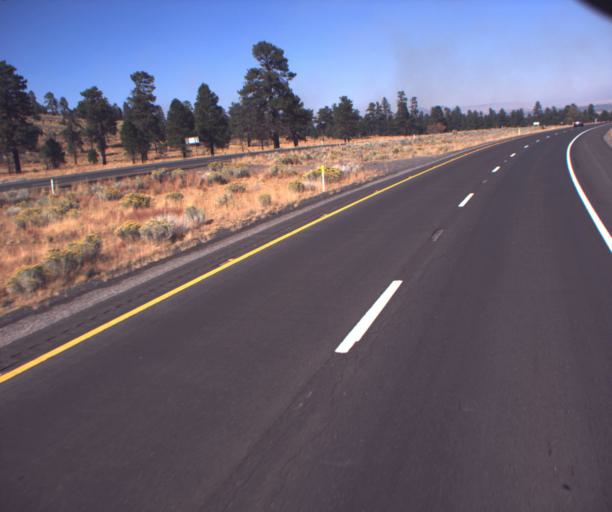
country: US
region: Arizona
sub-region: Coconino County
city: Flagstaff
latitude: 35.3822
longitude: -111.5805
